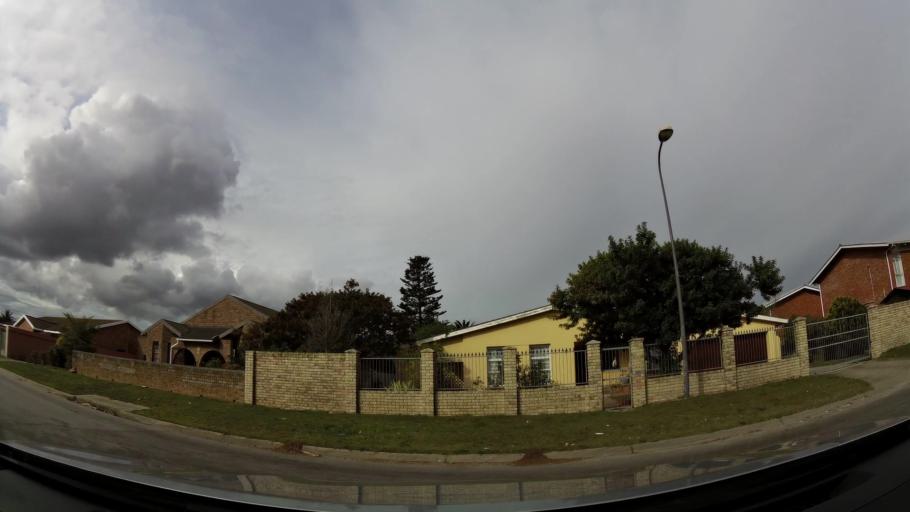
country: ZA
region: Eastern Cape
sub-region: Nelson Mandela Bay Metropolitan Municipality
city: Port Elizabeth
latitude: -33.9405
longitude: 25.5040
